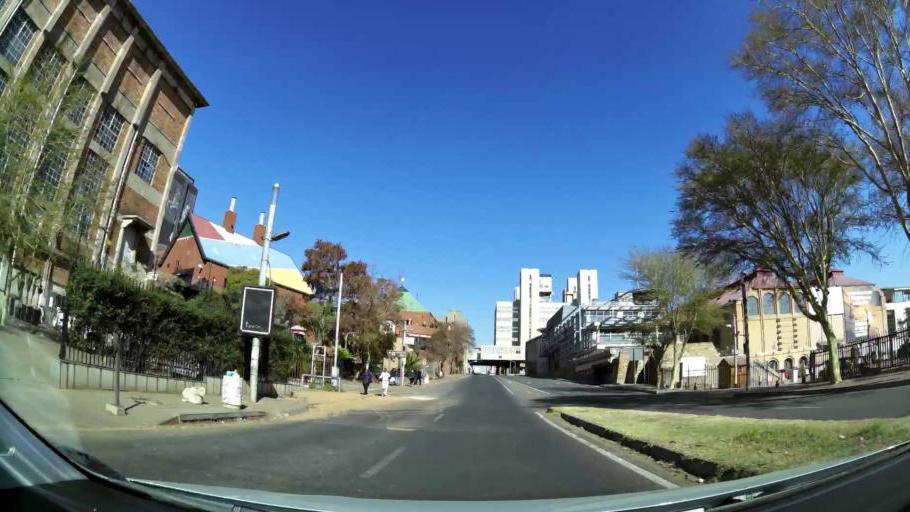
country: ZA
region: Gauteng
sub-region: City of Johannesburg Metropolitan Municipality
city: Johannesburg
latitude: -26.2035
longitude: 28.0335
